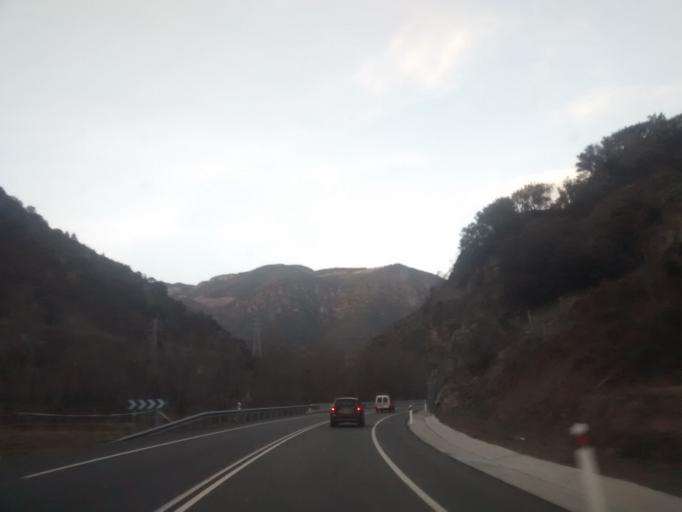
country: ES
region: Catalonia
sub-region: Provincia de Lleida
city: la Seu d'Urgell
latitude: 42.4139
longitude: 1.4646
